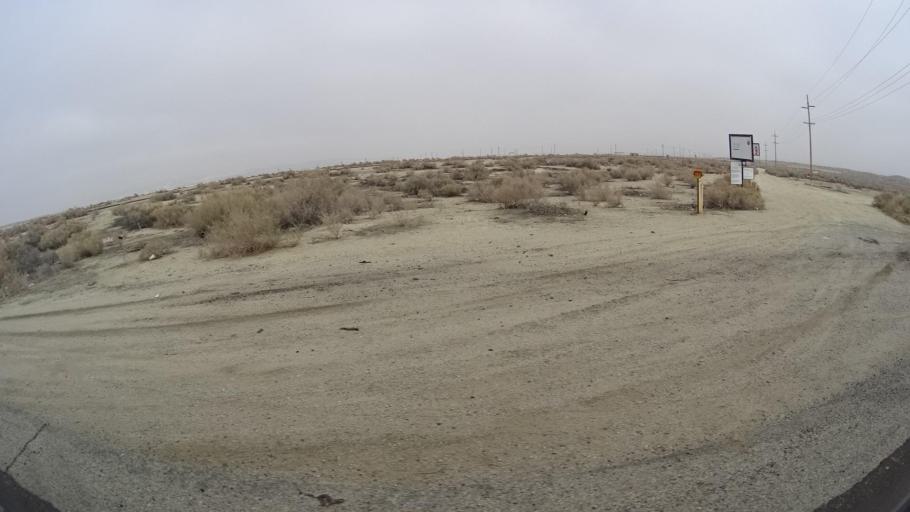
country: US
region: California
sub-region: Kern County
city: Maricopa
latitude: 35.0938
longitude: -119.4087
